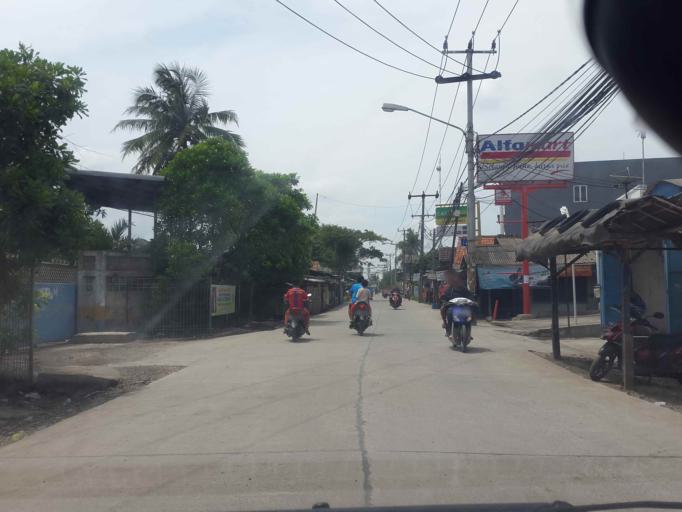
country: ID
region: West Java
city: Teluknaga
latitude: -6.1227
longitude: 106.6257
